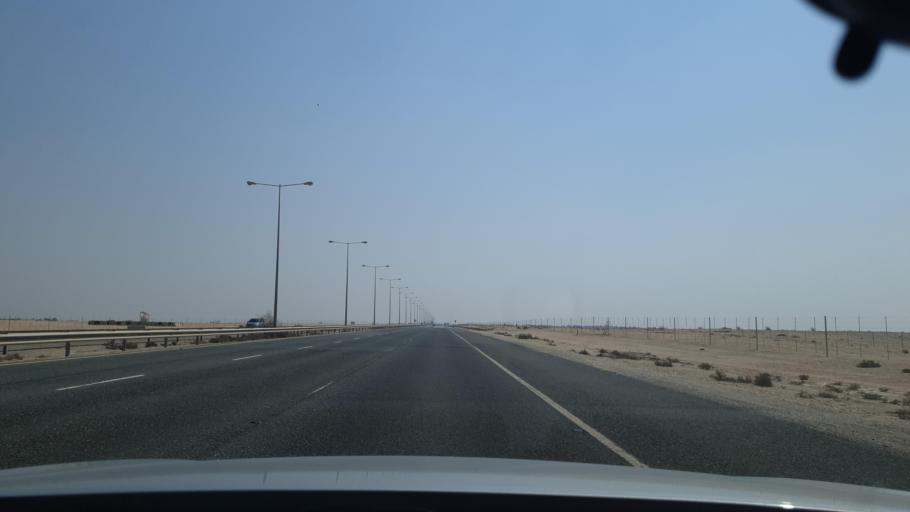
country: QA
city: Al Ghuwayriyah
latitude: 25.8048
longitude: 51.3790
